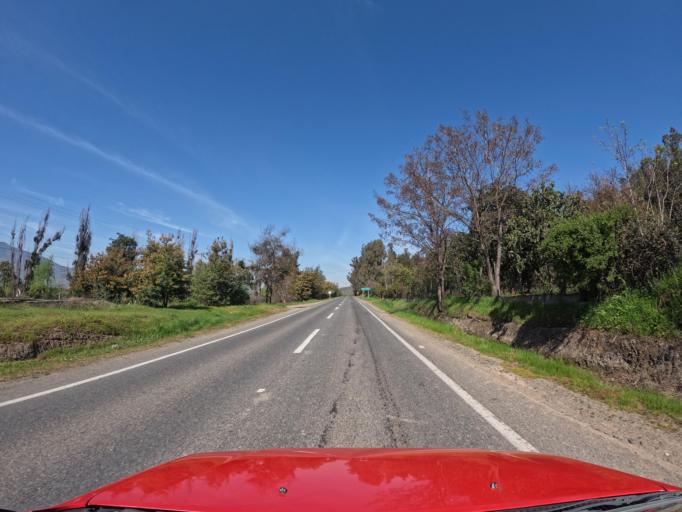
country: CL
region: Maule
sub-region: Provincia de Curico
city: Rauco
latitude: -35.0691
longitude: -71.6248
